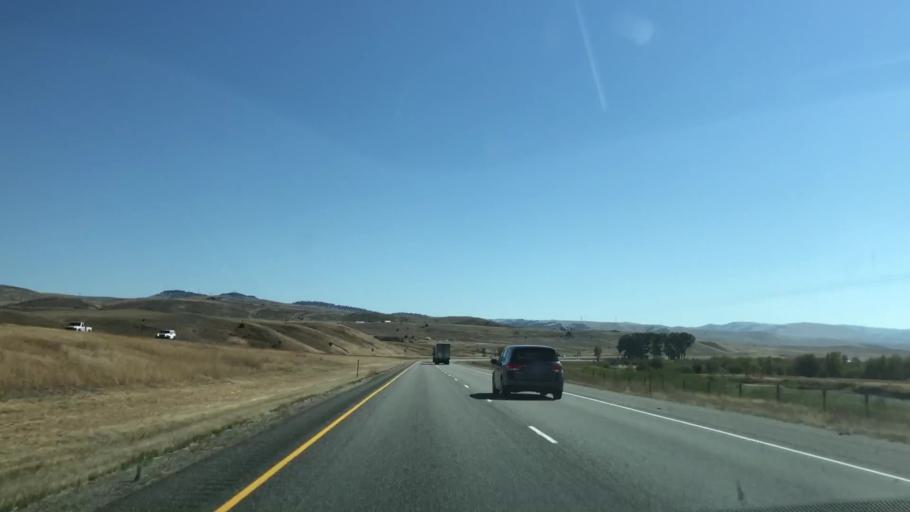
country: US
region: Montana
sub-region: Powell County
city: Deer Lodge
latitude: 46.5048
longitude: -112.7555
